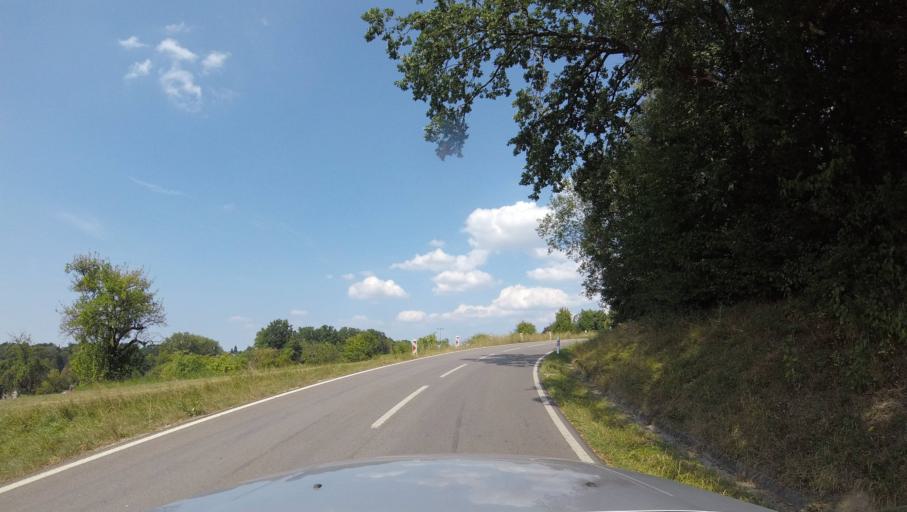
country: DE
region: Baden-Wuerttemberg
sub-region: Regierungsbezirk Stuttgart
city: Welzheim
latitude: 48.8729
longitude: 9.6464
